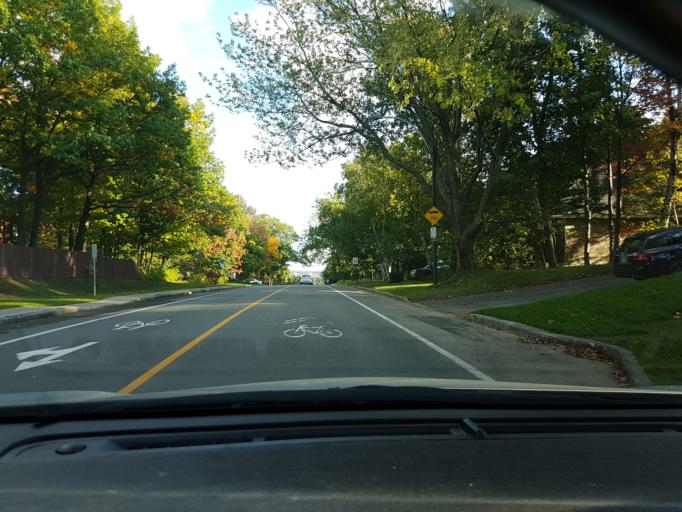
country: CA
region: Quebec
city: Quebec
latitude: 46.7718
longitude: -71.2697
